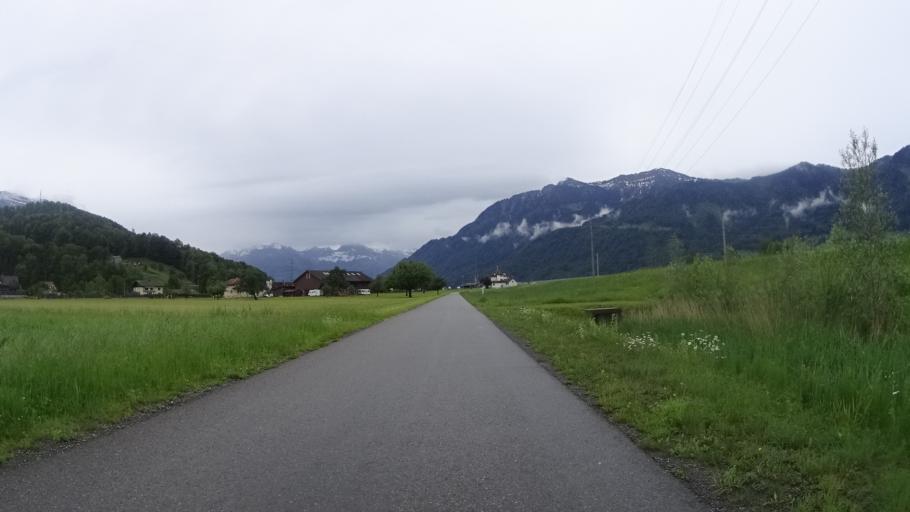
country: CH
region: Saint Gallen
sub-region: Wahlkreis See-Gaster
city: Benken
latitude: 47.1875
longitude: 8.9920
